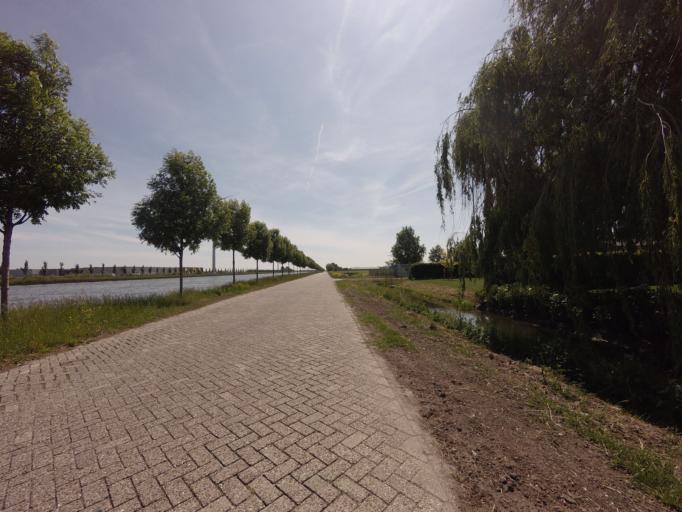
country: NL
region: Utrecht
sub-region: Gemeente Houten
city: Houten
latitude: 52.0208
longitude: 5.1362
